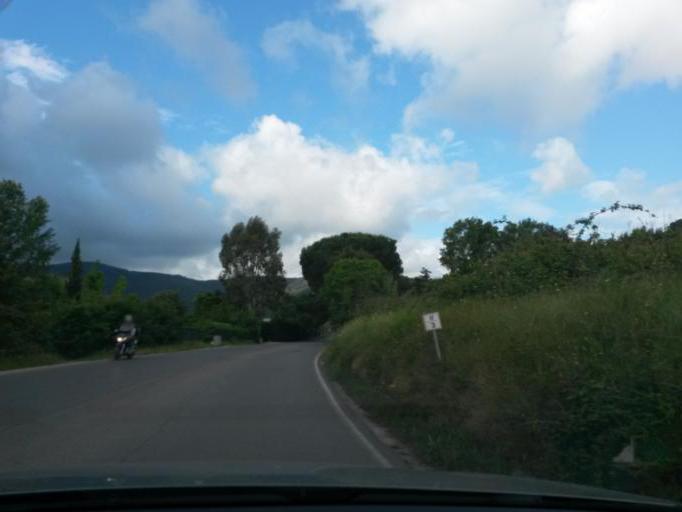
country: IT
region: Tuscany
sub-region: Provincia di Livorno
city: Portoferraio
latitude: 42.7973
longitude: 10.2996
